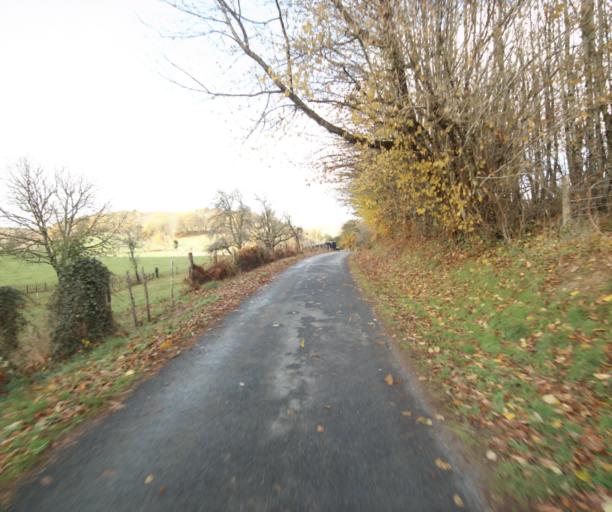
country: FR
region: Limousin
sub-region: Departement de la Correze
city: Chameyrat
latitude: 45.2259
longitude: 1.6887
